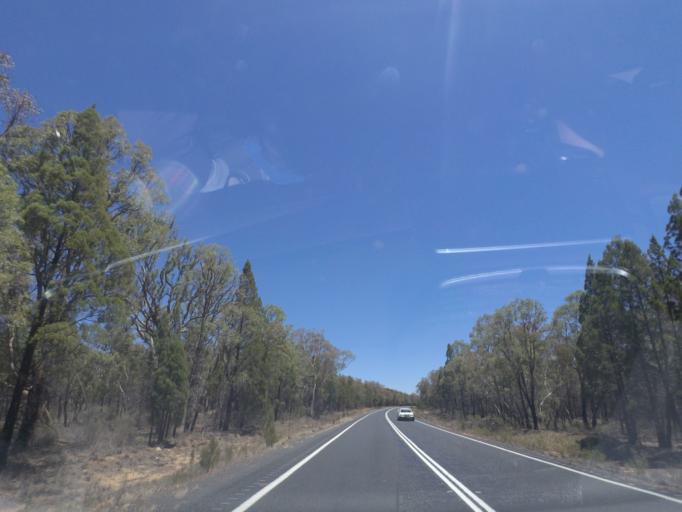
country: AU
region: New South Wales
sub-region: Warrumbungle Shire
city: Coonabarabran
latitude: -31.1963
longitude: 149.3503
